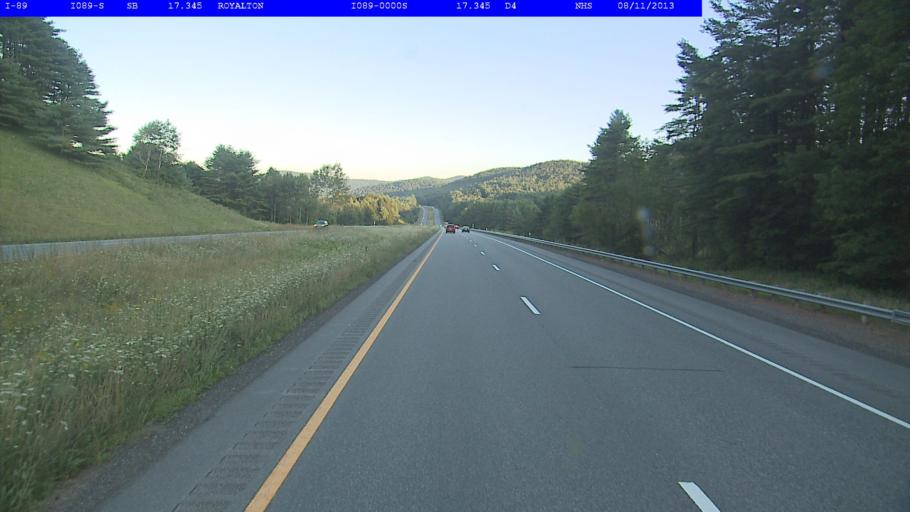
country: US
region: Vermont
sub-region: Windsor County
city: Woodstock
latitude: 43.8057
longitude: -72.5161
